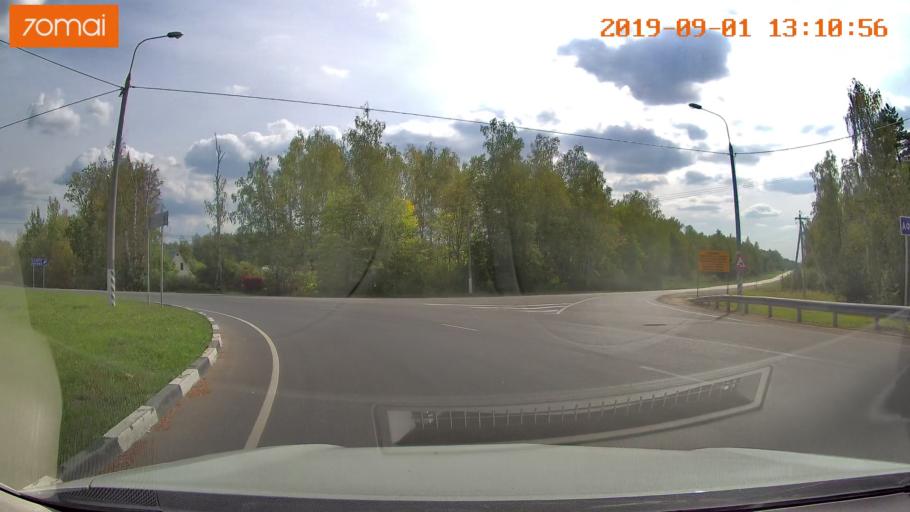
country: RU
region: Kaluga
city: Maloyaroslavets
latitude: 54.9797
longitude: 36.4250
